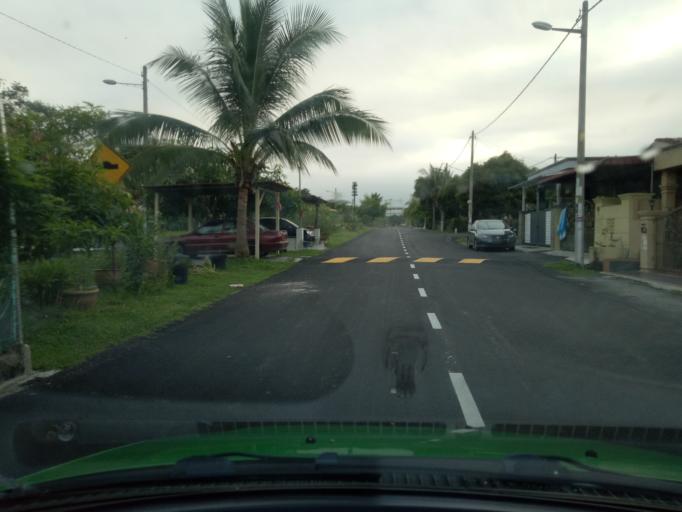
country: MY
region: Selangor
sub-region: Hulu Langat
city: Semenyih
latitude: 2.9298
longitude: 101.8598
